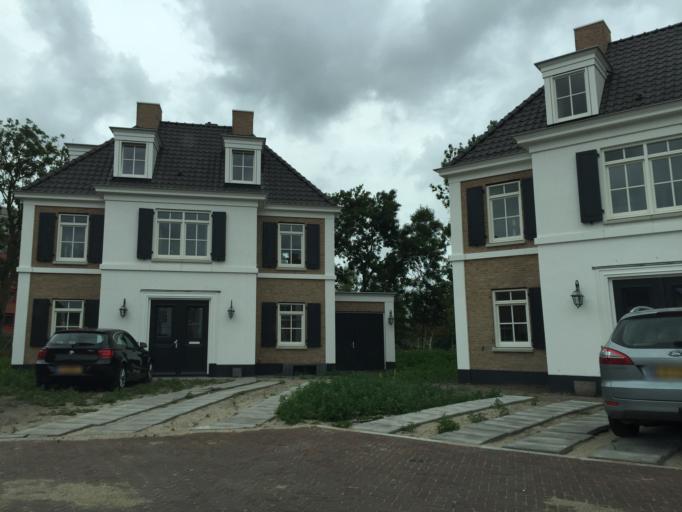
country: NL
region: South Holland
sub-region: Gemeente Pijnacker-Nootdorp
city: Pijnacker
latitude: 52.0049
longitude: 4.4508
